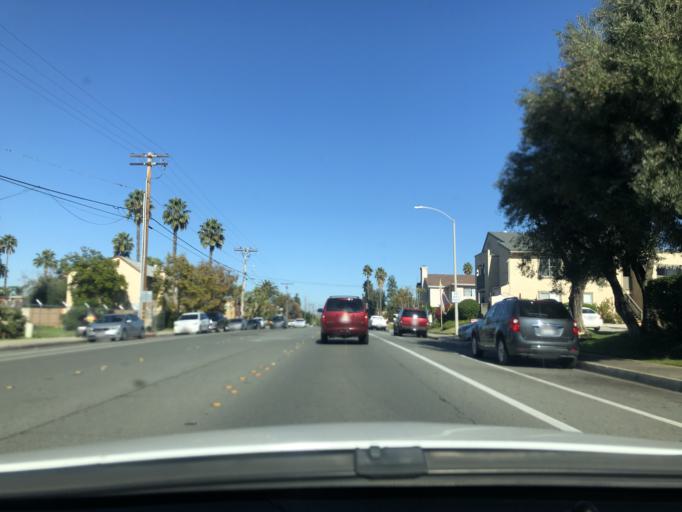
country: US
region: California
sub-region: San Diego County
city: El Cajon
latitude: 32.7811
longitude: -116.9510
